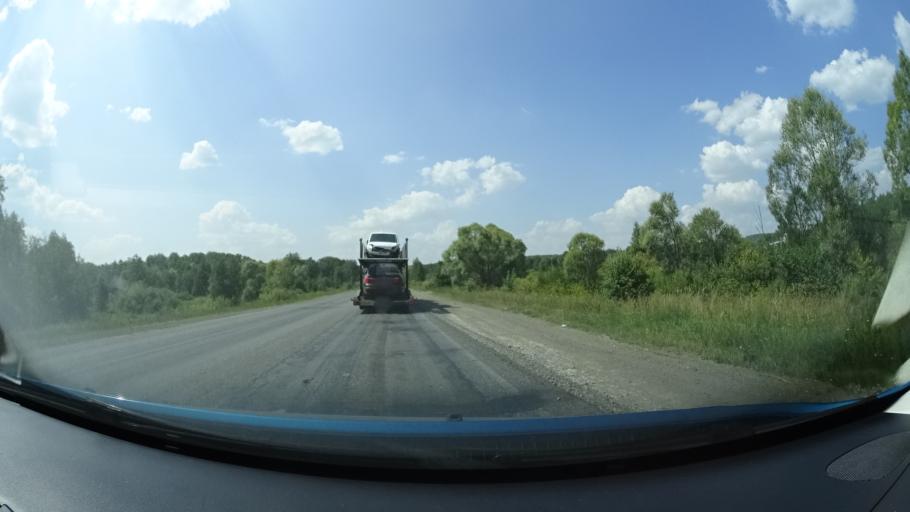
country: RU
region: Bashkortostan
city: Nizhnetroitskiy
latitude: 54.4502
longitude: 53.6290
